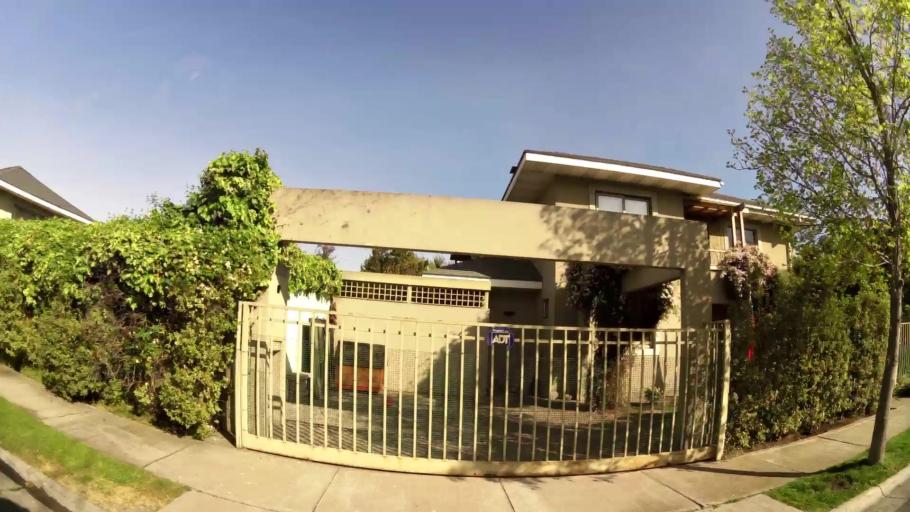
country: CL
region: Santiago Metropolitan
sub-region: Provincia de Santiago
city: Villa Presidente Frei, Nunoa, Santiago, Chile
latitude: -33.4892
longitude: -70.5525
